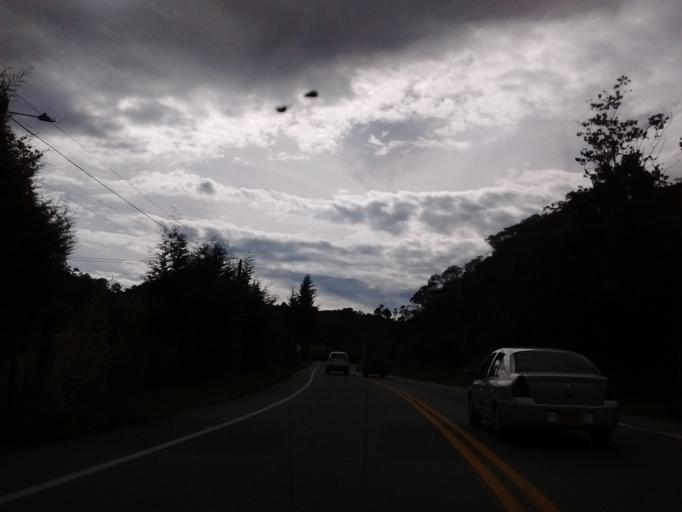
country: CO
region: Antioquia
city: Santuario
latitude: 6.0996
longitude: -75.2252
